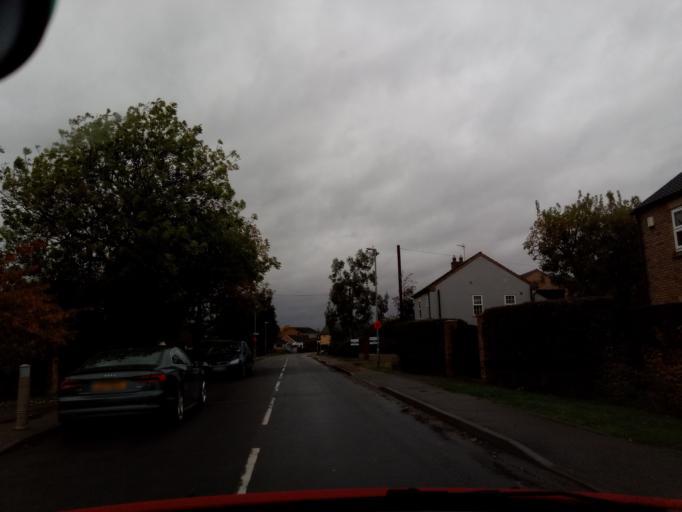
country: GB
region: England
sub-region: Cambridgeshire
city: Sawtry
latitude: 52.4332
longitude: -0.2790
